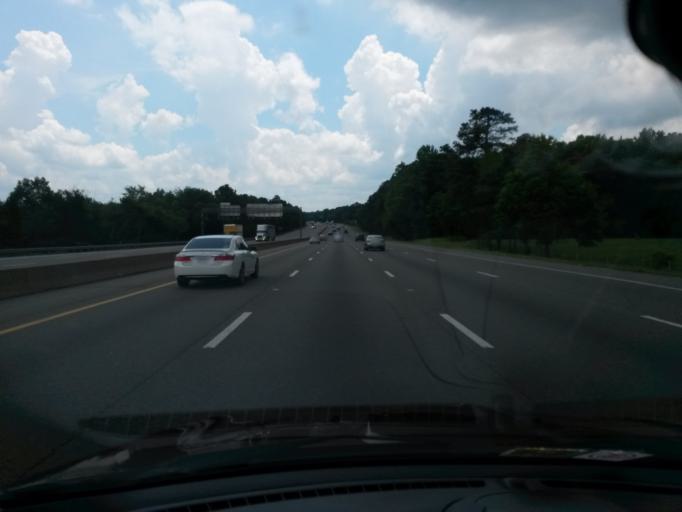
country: US
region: Virginia
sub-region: Chesterfield County
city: Bellwood
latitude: 37.3994
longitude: -77.4244
